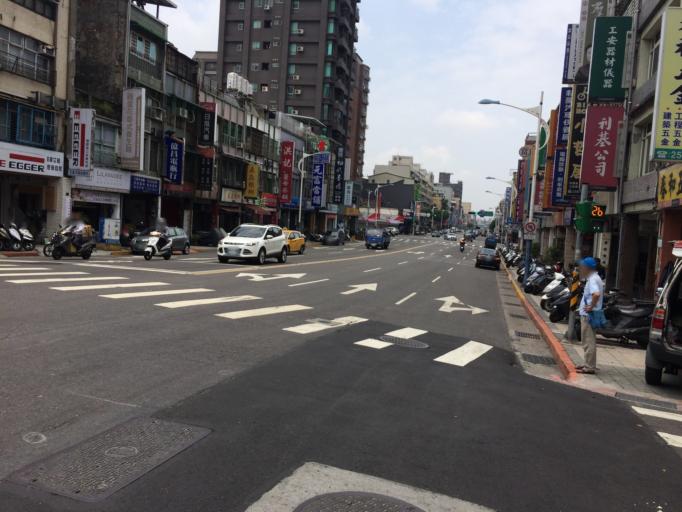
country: TW
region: Taipei
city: Taipei
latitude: 25.0686
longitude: 121.5196
